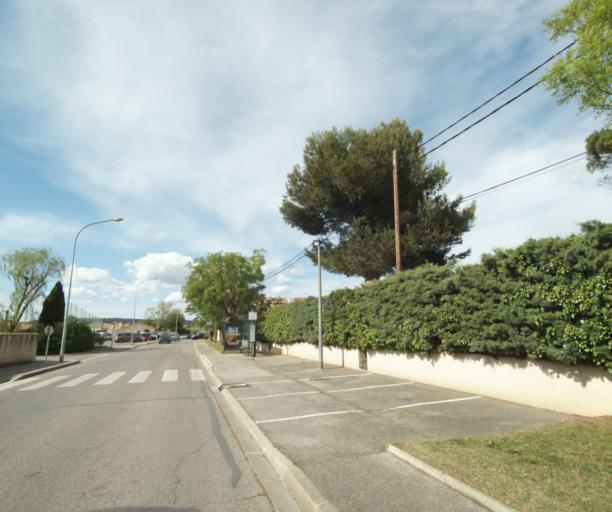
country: FR
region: Provence-Alpes-Cote d'Azur
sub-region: Departement des Bouches-du-Rhone
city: Rognac
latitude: 43.4913
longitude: 5.2218
